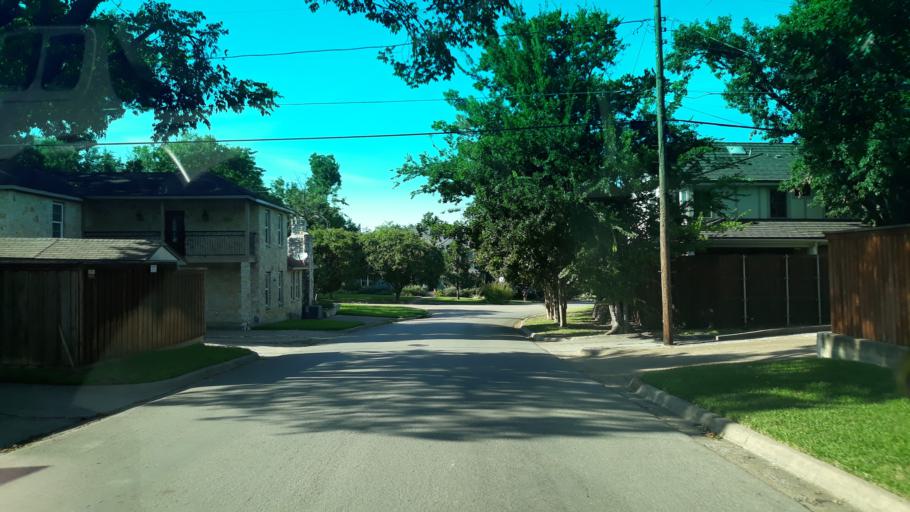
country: US
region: Texas
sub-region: Dallas County
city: Highland Park
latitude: 32.8296
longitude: -96.7559
